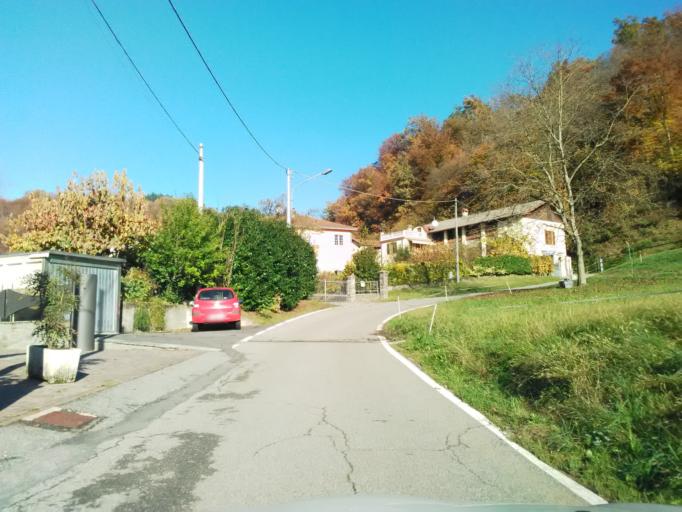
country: IT
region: Piedmont
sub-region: Provincia di Vercelli
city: Borgosesia
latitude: 45.7322
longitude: 8.2852
